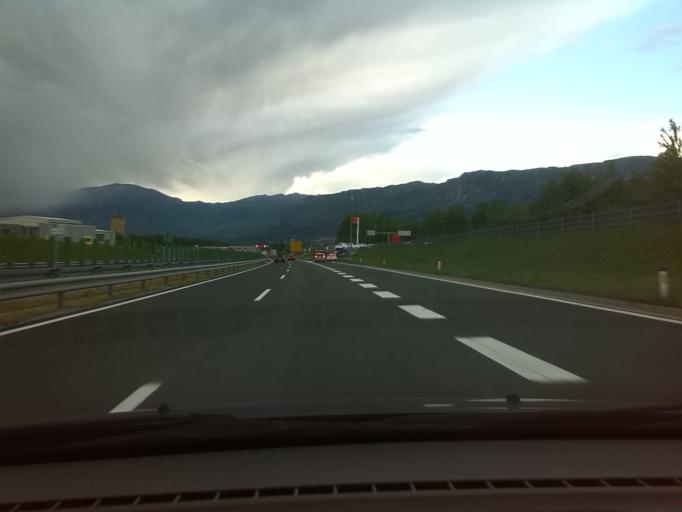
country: SI
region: Vipava
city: Vipava
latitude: 45.8273
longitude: 13.9593
